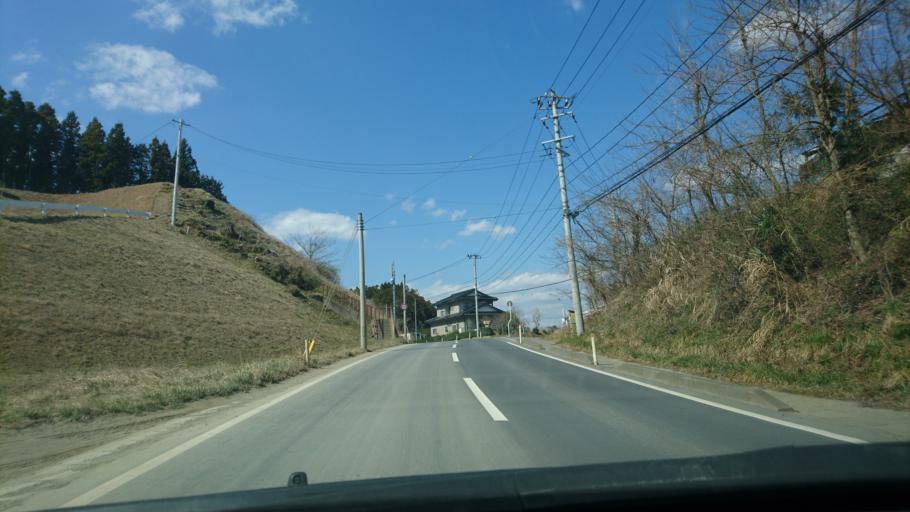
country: JP
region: Miyagi
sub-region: Oshika Gun
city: Onagawa Cho
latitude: 38.6401
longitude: 141.4541
